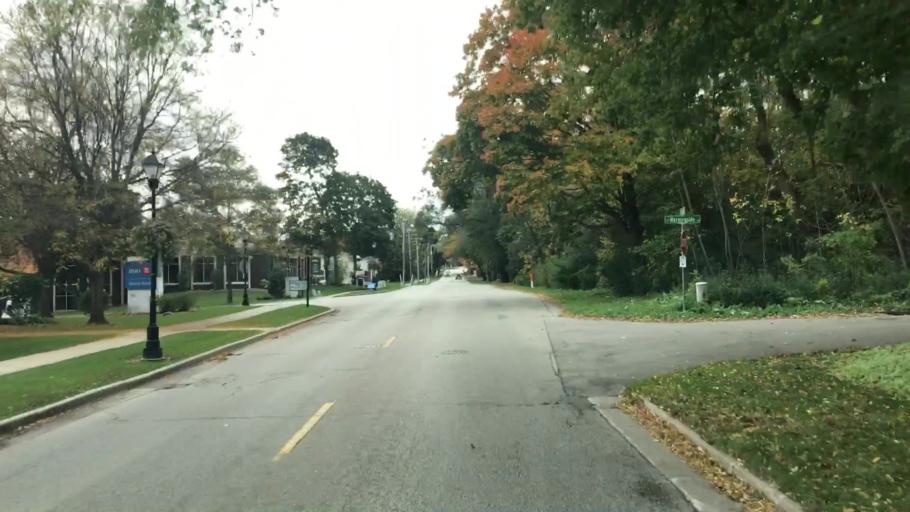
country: US
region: Wisconsin
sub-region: Waukesha County
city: Elm Grove
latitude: 43.0409
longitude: -88.0796
